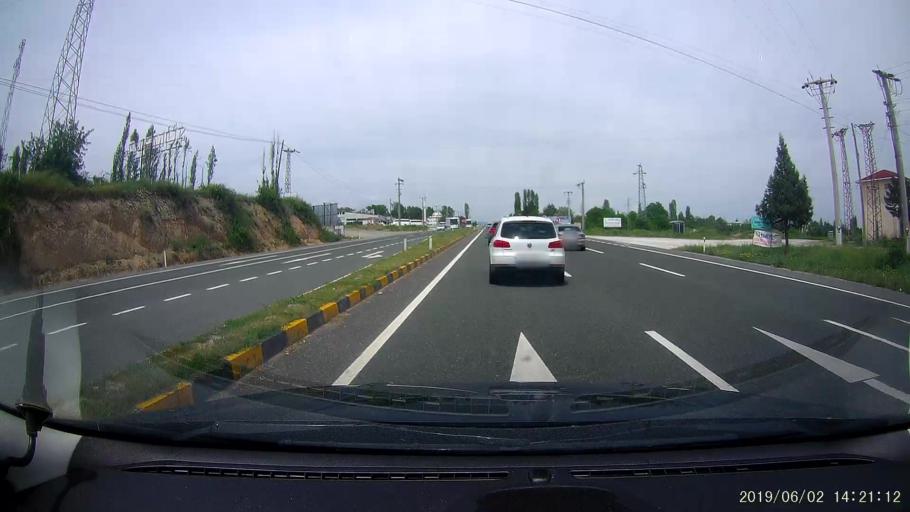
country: TR
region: Kastamonu
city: Tosya
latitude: 40.9768
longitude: 34.0004
